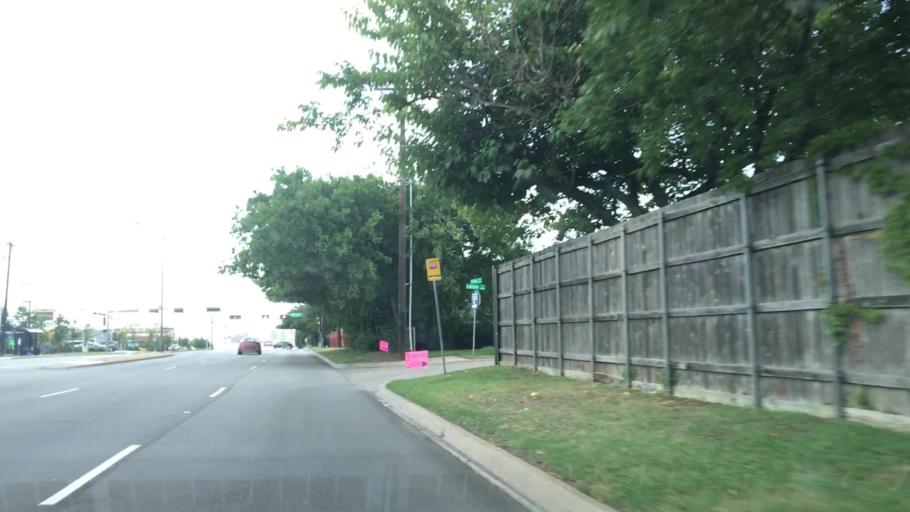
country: US
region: Texas
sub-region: Dallas County
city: Addison
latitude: 32.9205
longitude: -96.8381
